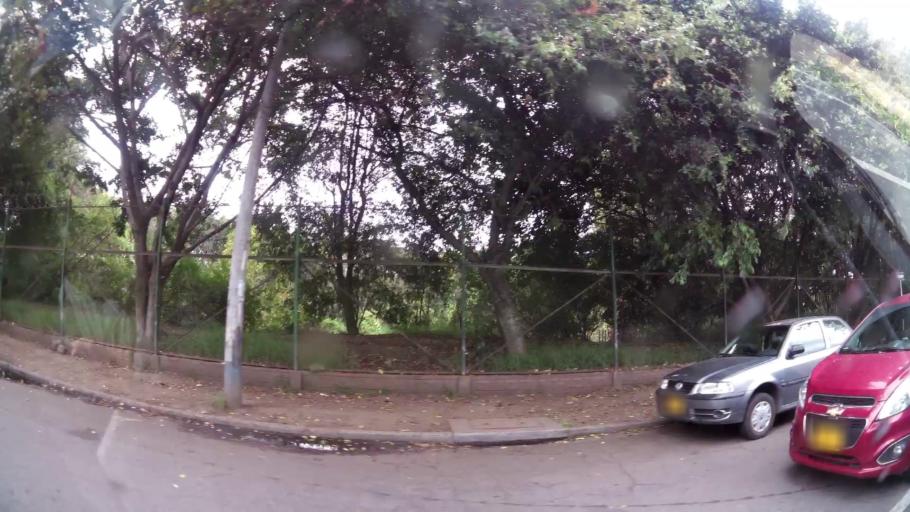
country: CO
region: Bogota D.C.
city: Barrio San Luis
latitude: 4.6932
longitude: -74.0963
